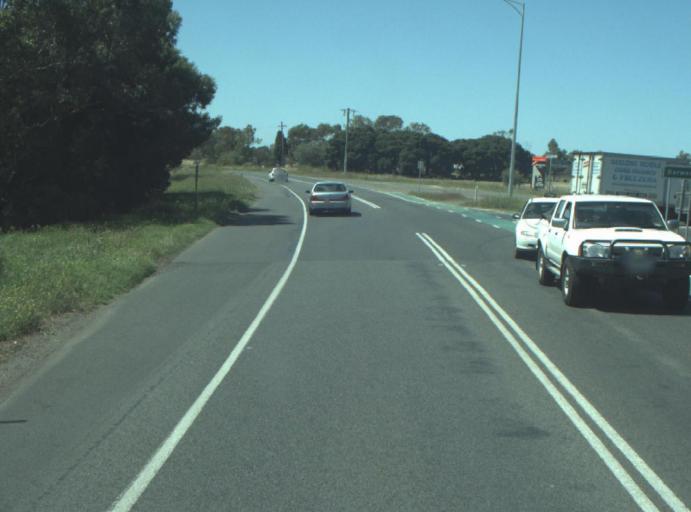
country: AU
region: Victoria
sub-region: Greater Geelong
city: Breakwater
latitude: -38.1864
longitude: 144.3547
